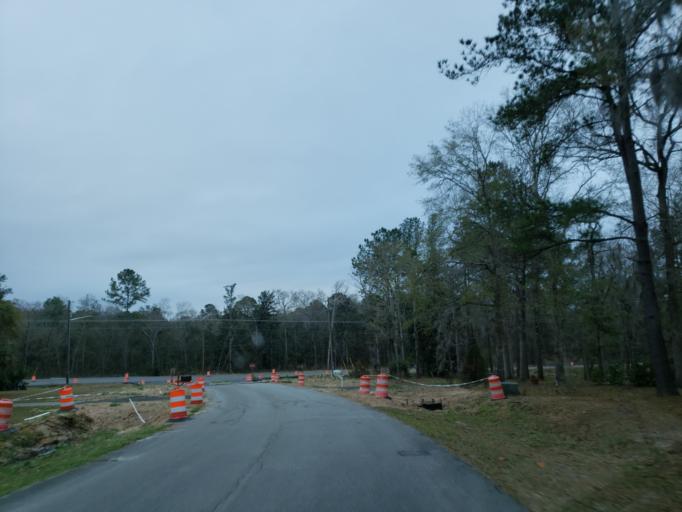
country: US
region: Georgia
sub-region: Lowndes County
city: Remerton
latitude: 30.8948
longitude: -83.3641
